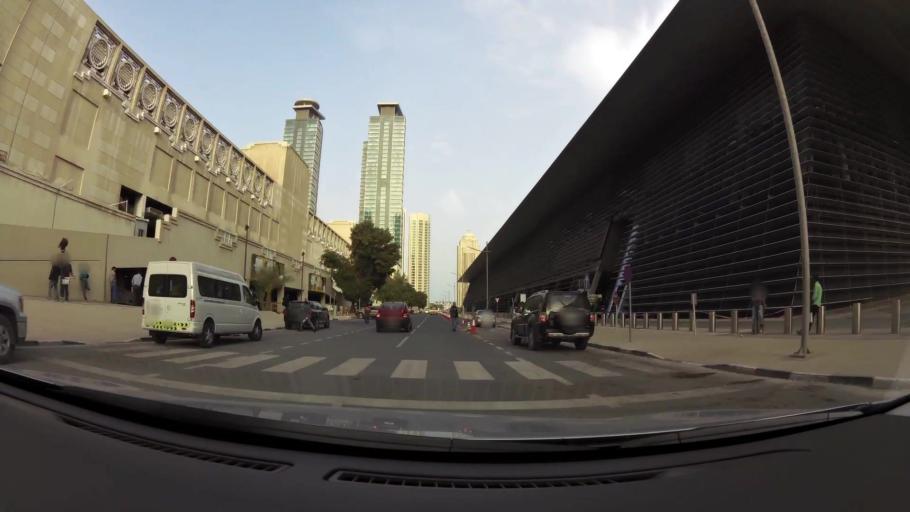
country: QA
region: Baladiyat ad Dawhah
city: Doha
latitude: 25.3241
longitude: 51.5293
